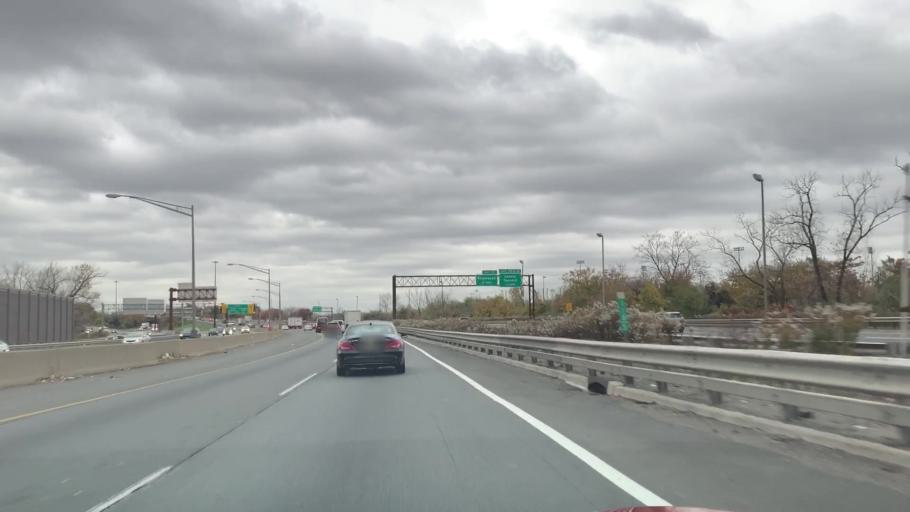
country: US
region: New Jersey
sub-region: Bergen County
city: Ridgefield Park
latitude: 40.8581
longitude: -74.0121
